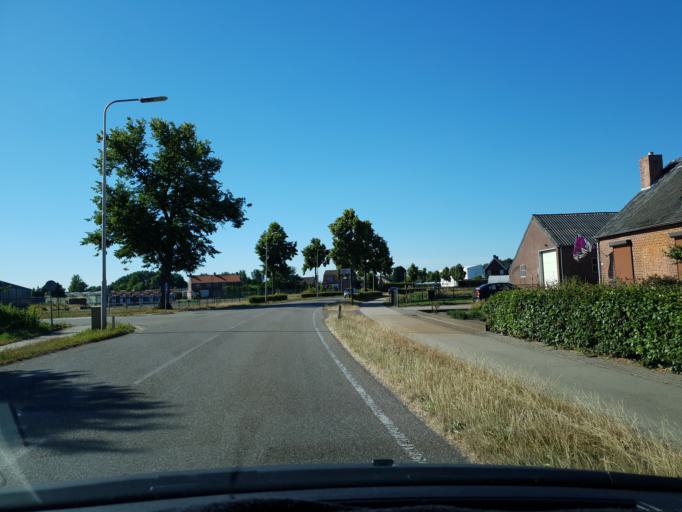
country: NL
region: North Brabant
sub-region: Gemeente Zundert
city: Zundert
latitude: 51.4692
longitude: 4.6838
